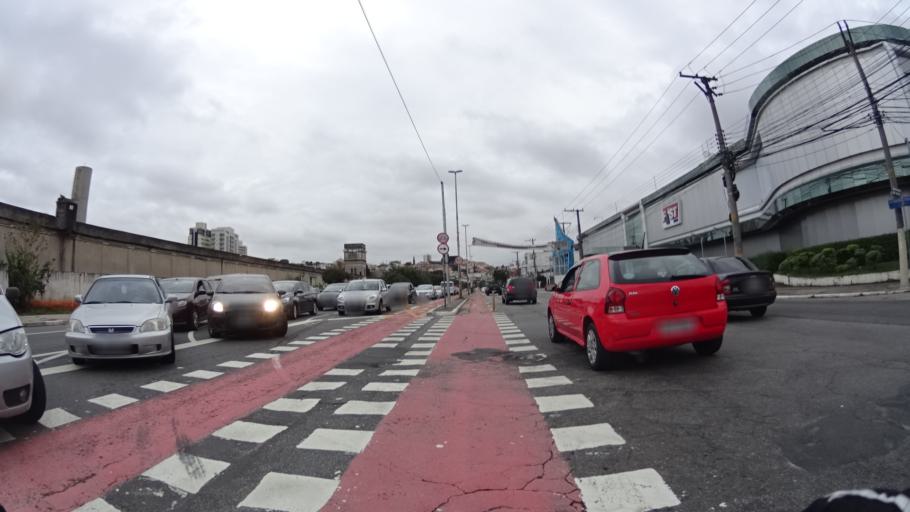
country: BR
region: Sao Paulo
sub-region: Sao Paulo
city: Sao Paulo
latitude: -23.5038
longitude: -46.6152
